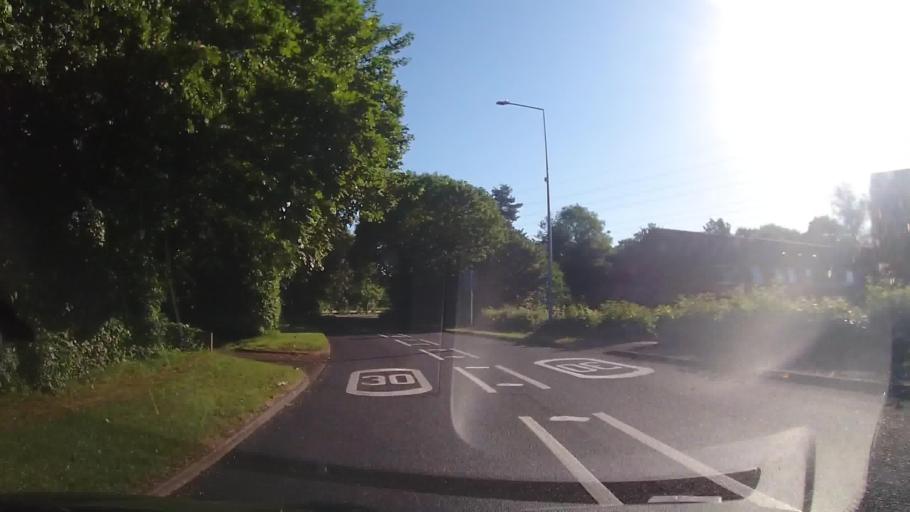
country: GB
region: England
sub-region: Shropshire
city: Hadley
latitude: 52.7069
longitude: -2.4942
